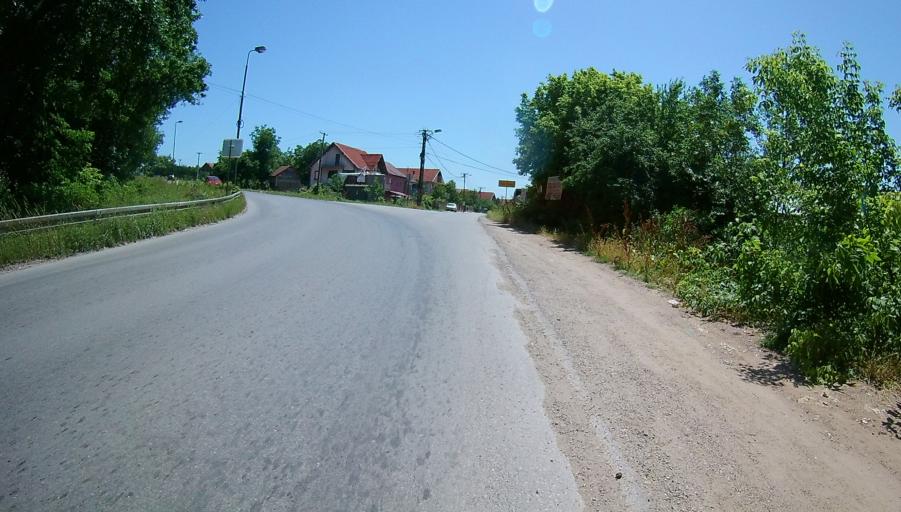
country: RS
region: Central Serbia
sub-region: Nisavski Okrug
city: Nis
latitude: 43.3054
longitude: 21.8674
